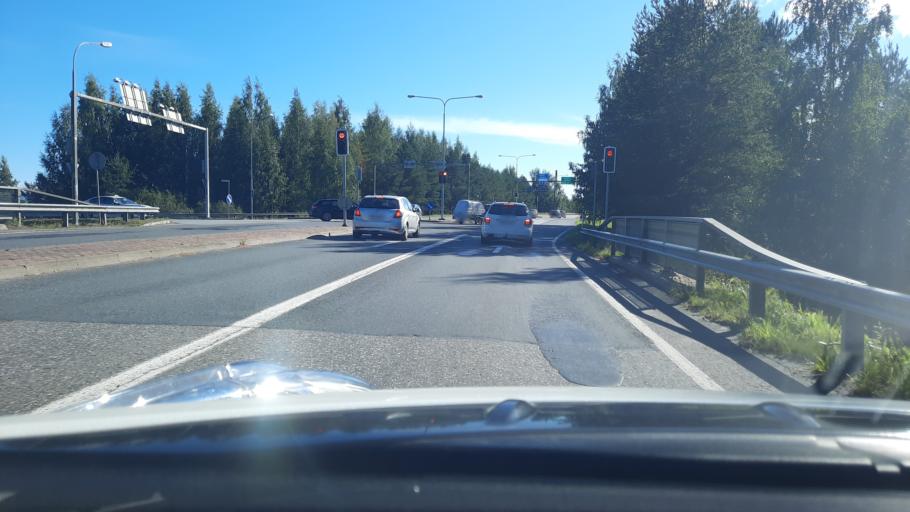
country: FI
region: North Karelia
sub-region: Joensuu
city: Joensuu
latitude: 62.6310
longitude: 29.7003
